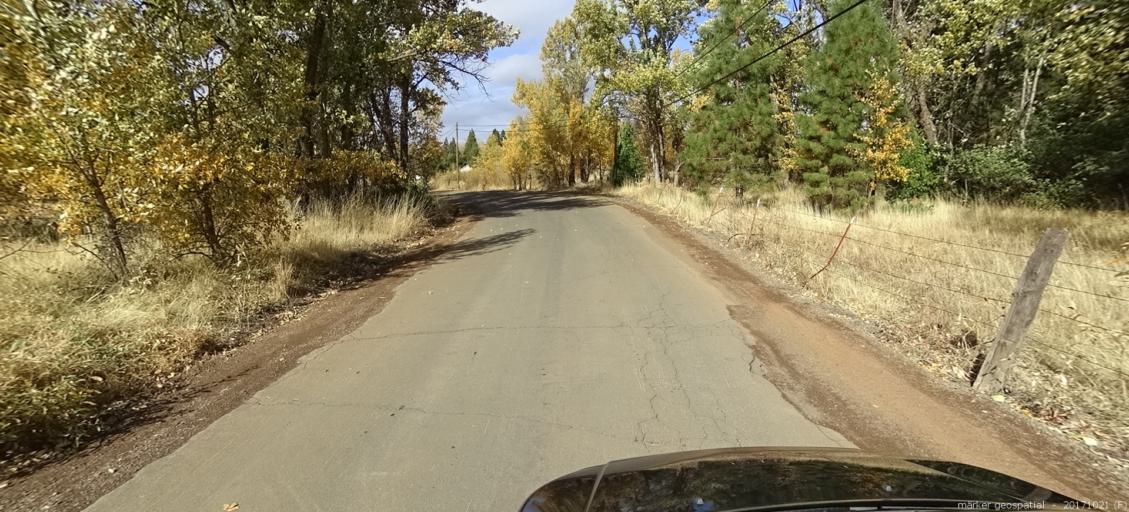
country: US
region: California
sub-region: Shasta County
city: Burney
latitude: 40.8860
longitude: -121.6688
